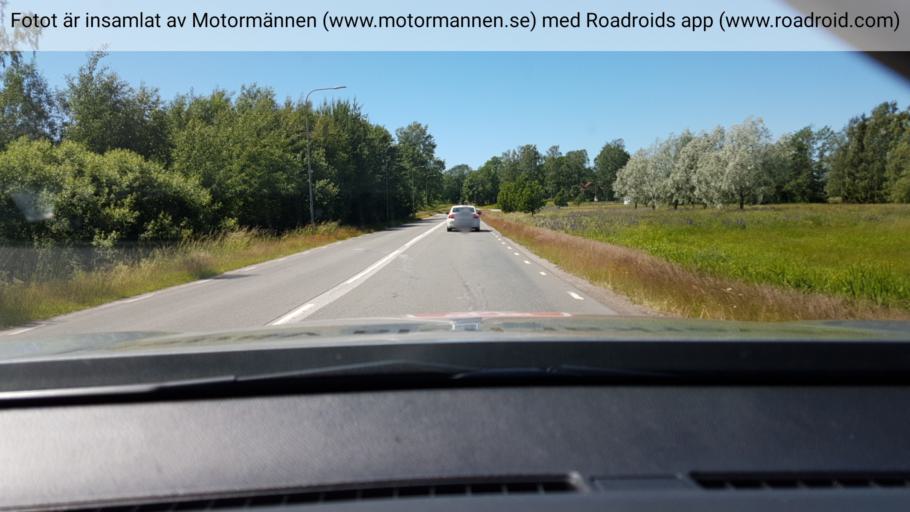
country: SE
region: Vaestra Goetaland
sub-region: Toreboda Kommun
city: Toereboda
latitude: 58.8302
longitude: 13.9885
